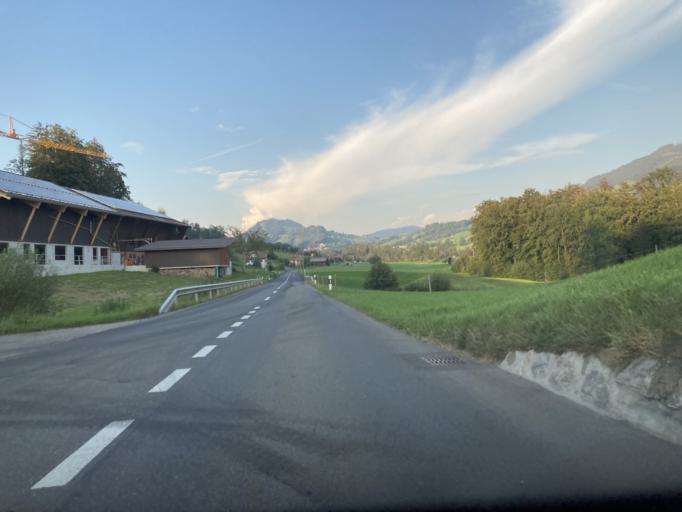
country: CH
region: Schwyz
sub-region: Bezirk Schwyz
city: Steinen
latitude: 47.0637
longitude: 8.6080
